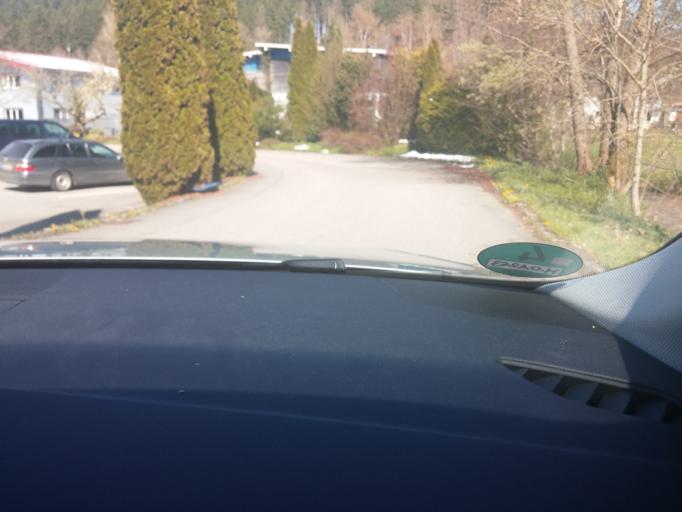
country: DE
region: Baden-Wuerttemberg
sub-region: Tuebingen Region
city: Rot an der Rot
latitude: 47.9813
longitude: 10.0429
